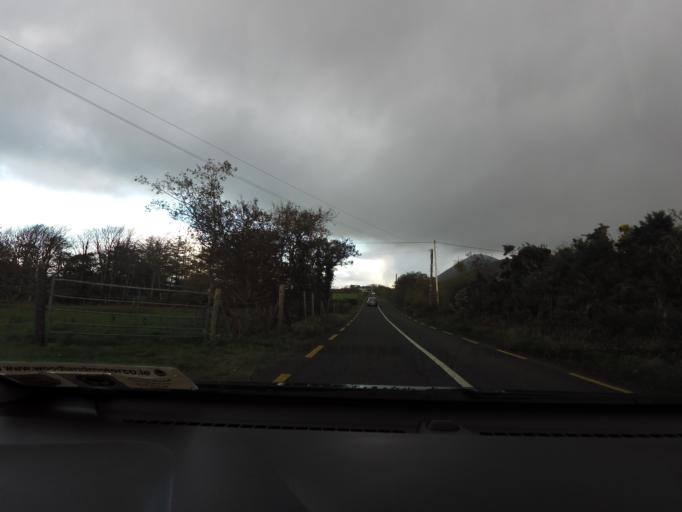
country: IE
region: Connaught
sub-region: Maigh Eo
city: Westport
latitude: 53.7723
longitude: -9.7445
